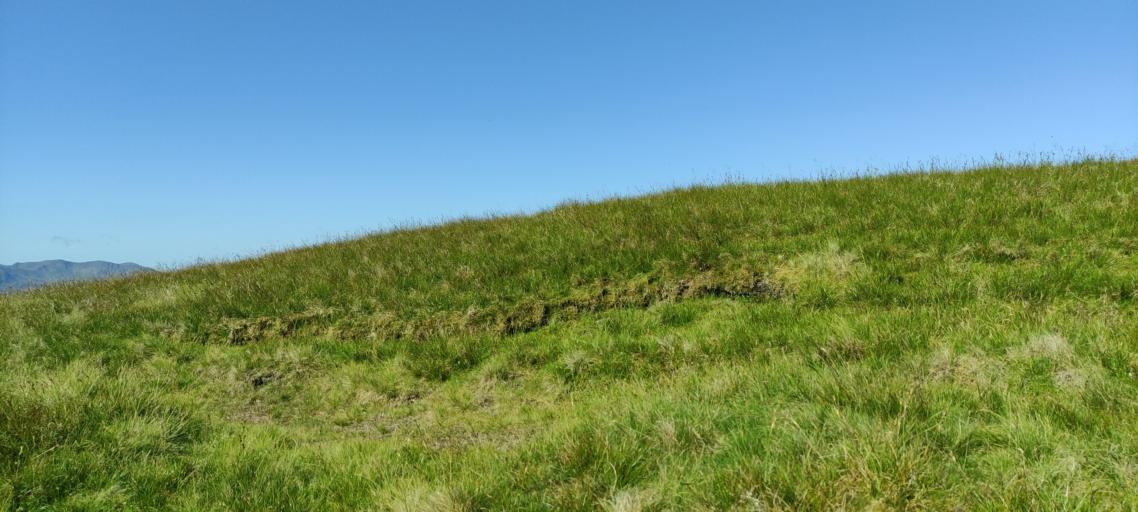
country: GB
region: England
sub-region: Cumbria
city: Ambleside
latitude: 54.4770
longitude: -2.9952
